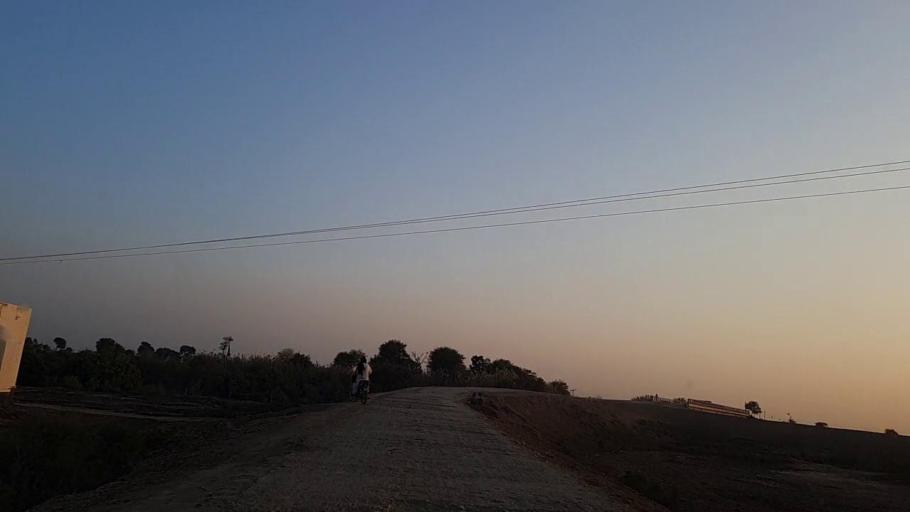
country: PK
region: Sindh
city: Bhit Shah
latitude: 25.9162
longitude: 68.5061
